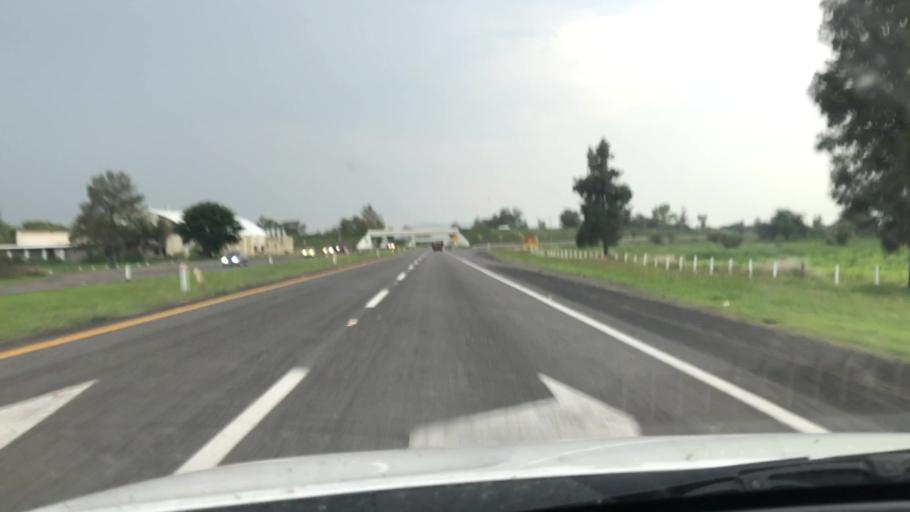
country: MX
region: Jalisco
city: La Barca
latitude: 20.3221
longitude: -102.5330
